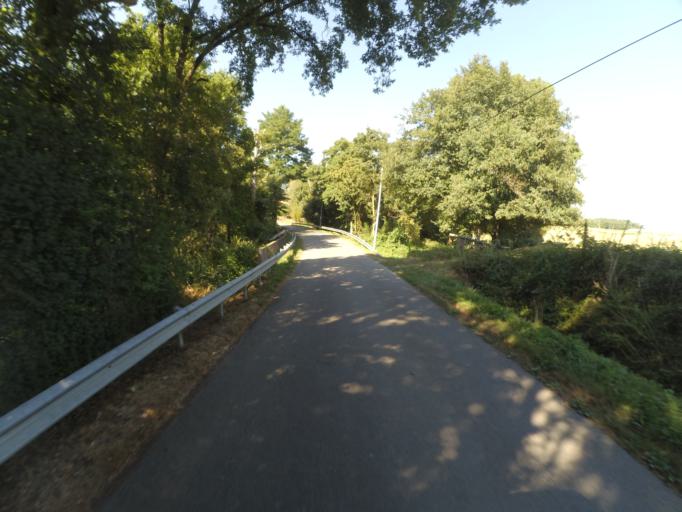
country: FR
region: Pays de la Loire
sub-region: Departement de la Loire-Atlantique
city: Vallet
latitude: 47.1969
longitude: -1.2643
